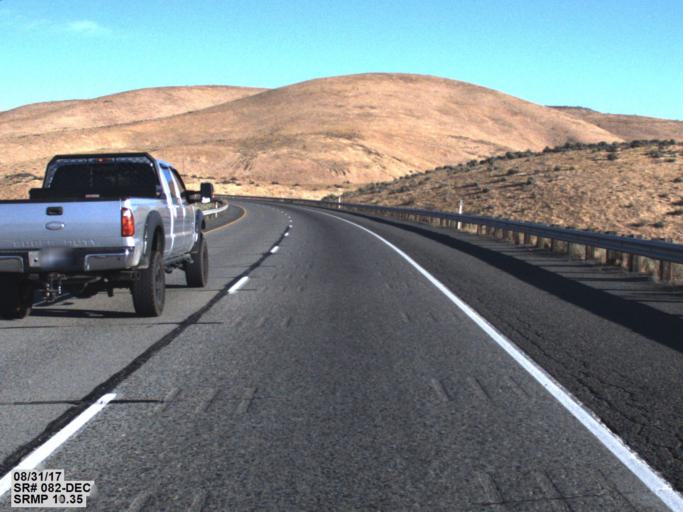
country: US
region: Washington
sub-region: Kittitas County
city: Kittitas
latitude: 46.8576
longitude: -120.3932
